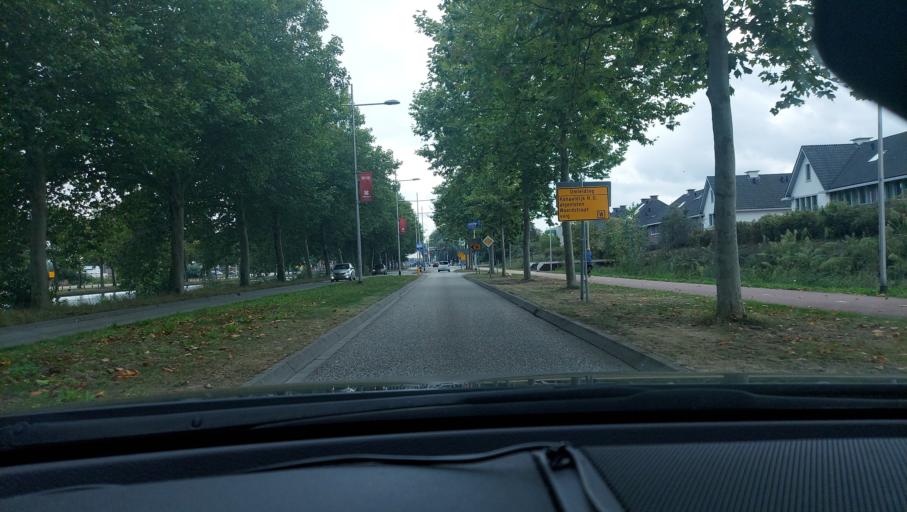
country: NL
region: North Brabant
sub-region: Gemeente Helmond
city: Helmond
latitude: 51.4877
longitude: 5.6514
